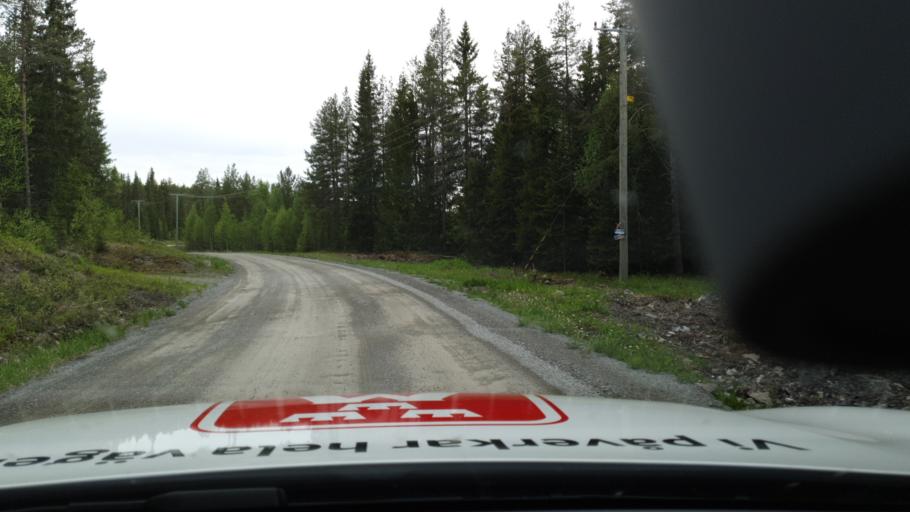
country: SE
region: Jaemtland
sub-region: OEstersunds Kommun
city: Brunflo
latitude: 62.9956
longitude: 14.7341
